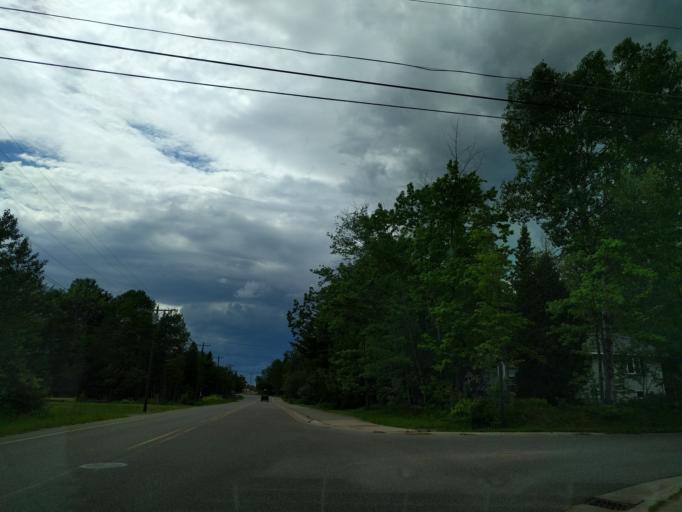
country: US
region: Michigan
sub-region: Marquette County
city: Trowbridge Park
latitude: 46.5516
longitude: -87.4451
